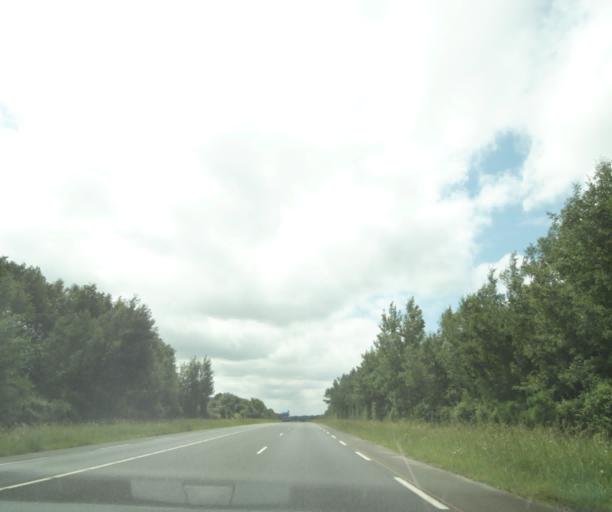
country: FR
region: Poitou-Charentes
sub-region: Departement des Deux-Sevres
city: Airvault
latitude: 46.7954
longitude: -0.2136
